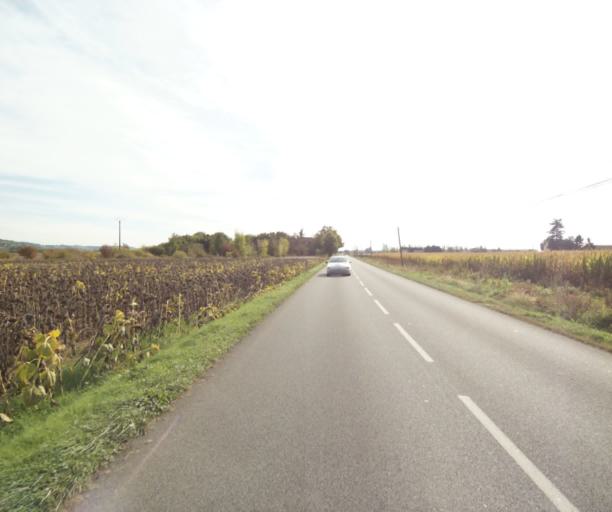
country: FR
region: Midi-Pyrenees
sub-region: Departement du Tarn-et-Garonne
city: Corbarieu
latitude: 43.9340
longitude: 1.3797
